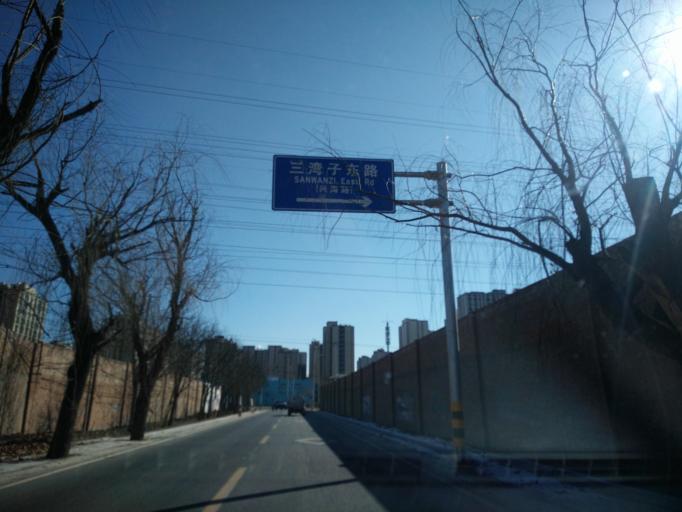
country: CN
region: Beijing
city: Yinghai
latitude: 39.7524
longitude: 116.4743
